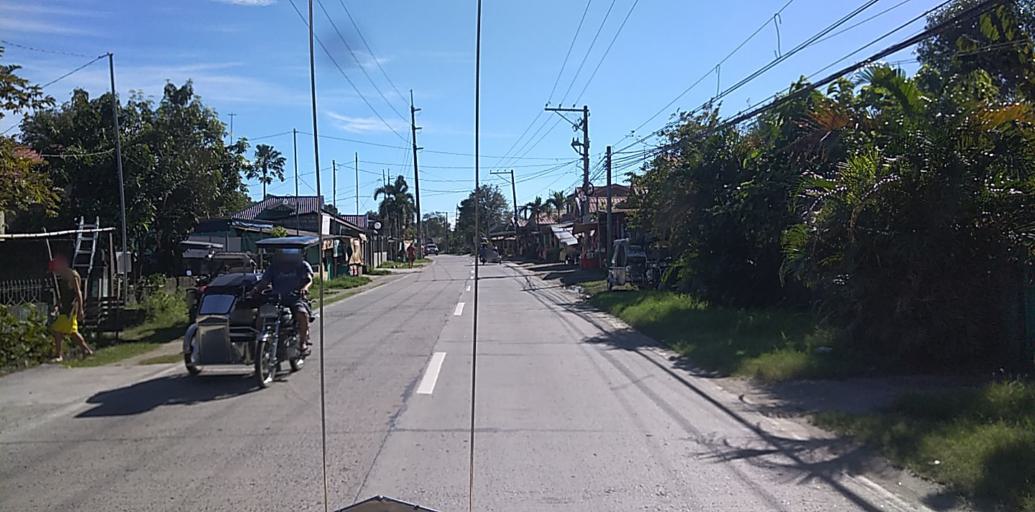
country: PH
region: Central Luzon
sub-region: Province of Pampanga
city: Santo Domingo
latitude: 15.0725
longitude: 120.7594
